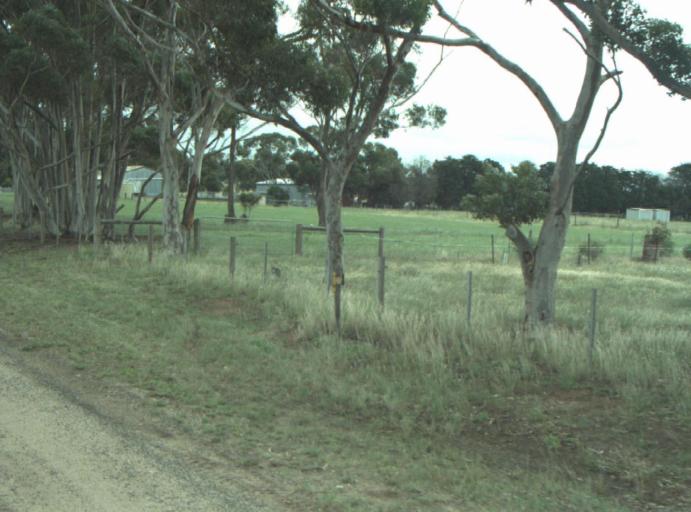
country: AU
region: Victoria
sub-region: Greater Geelong
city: Lara
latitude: -37.9764
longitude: 144.4235
